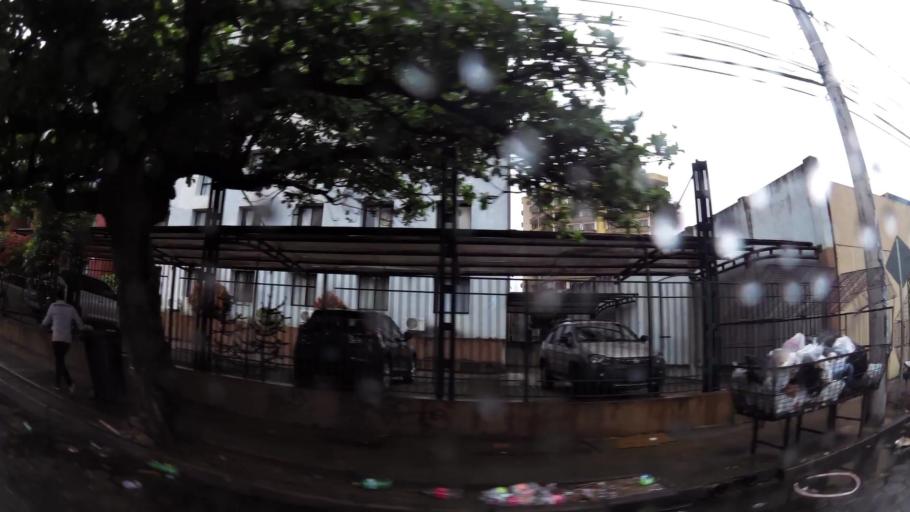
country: BO
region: Santa Cruz
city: Santa Cruz de la Sierra
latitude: -17.7747
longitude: -63.1673
